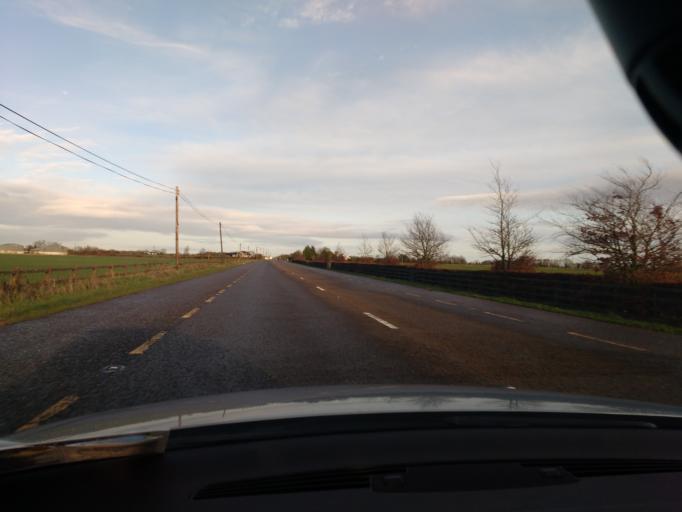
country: IE
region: Munster
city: Thurles
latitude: 52.6643
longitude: -7.6937
